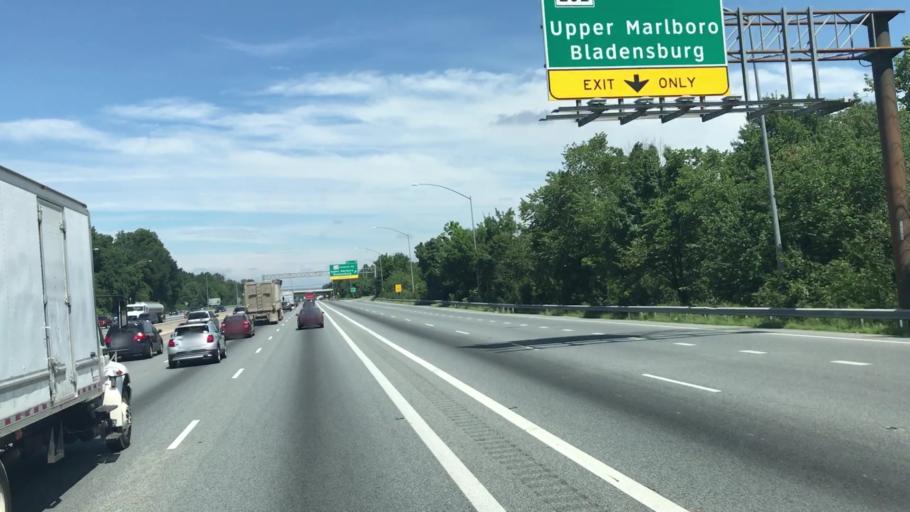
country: US
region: Maryland
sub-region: Prince George's County
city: Lake Arbor
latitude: 38.9115
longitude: -76.8498
